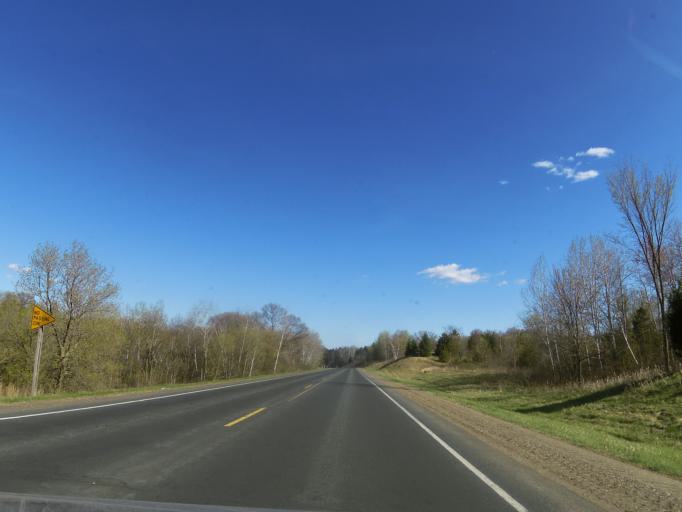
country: US
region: Minnesota
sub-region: Washington County
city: Bayport
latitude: 45.0529
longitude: -92.7234
